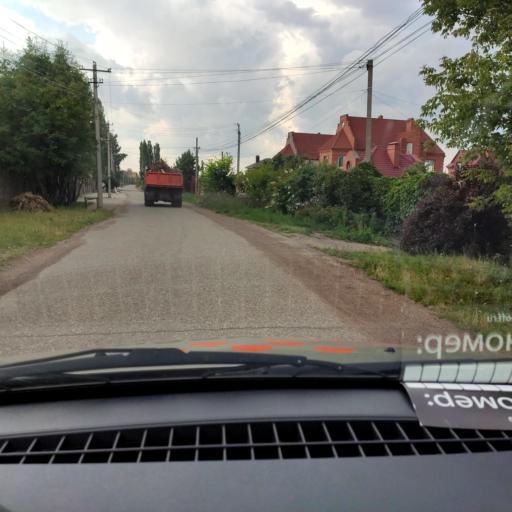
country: RU
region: Bashkortostan
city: Ufa
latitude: 54.6196
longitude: 55.9188
